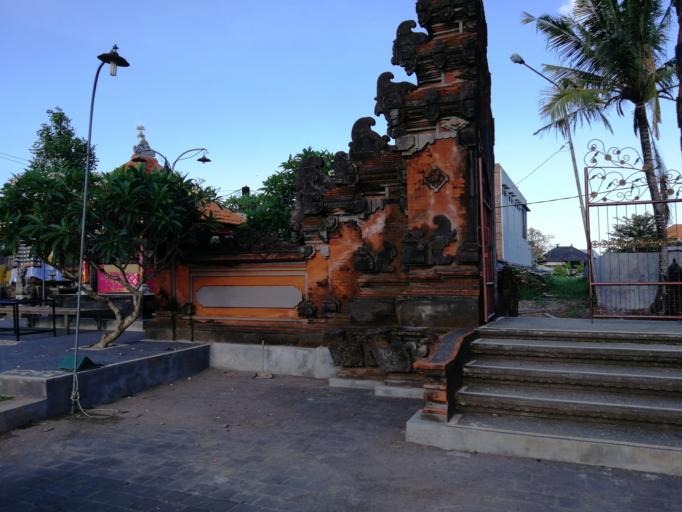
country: ID
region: Bali
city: Banjar Gunungpande
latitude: -8.6103
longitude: 115.1568
